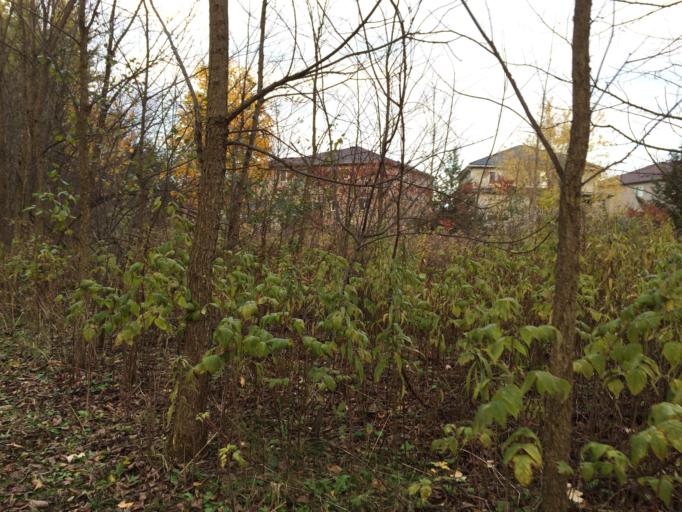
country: CA
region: Ontario
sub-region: Wellington County
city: Guelph
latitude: 43.5267
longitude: -80.3045
